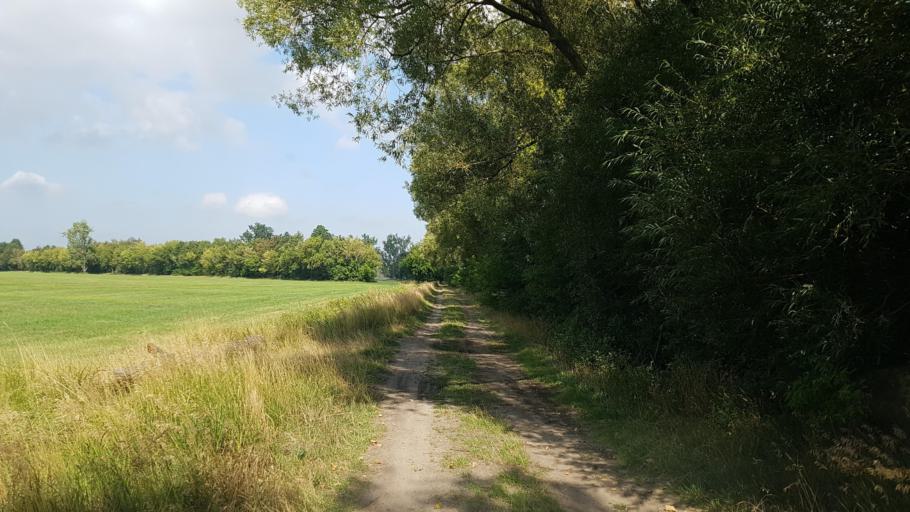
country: DE
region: Brandenburg
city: Borkheide
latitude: 52.1949
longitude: 12.8134
